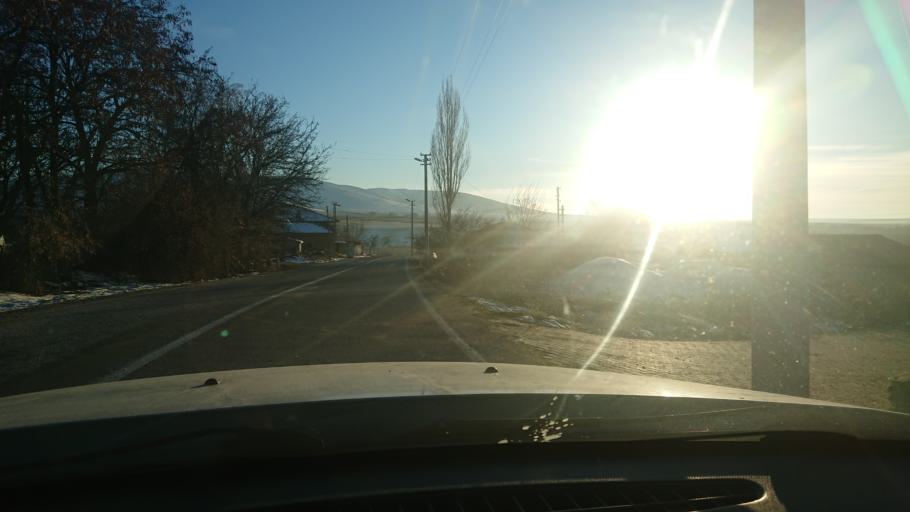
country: TR
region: Aksaray
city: Ortakoy
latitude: 38.7563
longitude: 33.9342
